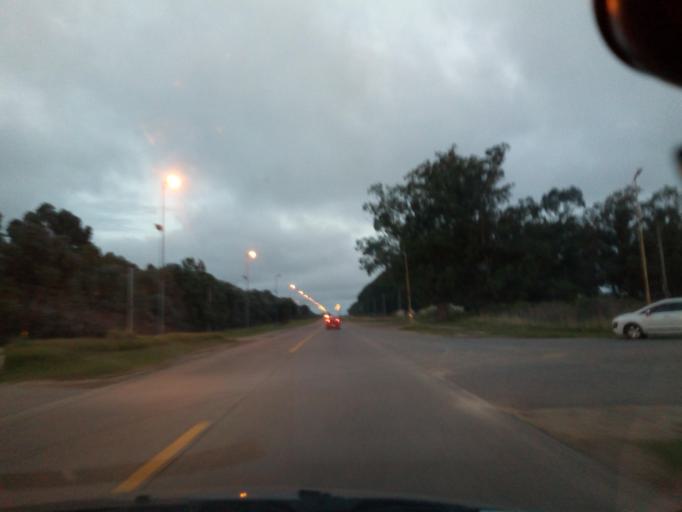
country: AR
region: Buenos Aires
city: Mar del Plata
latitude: -38.0792
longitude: -57.5836
